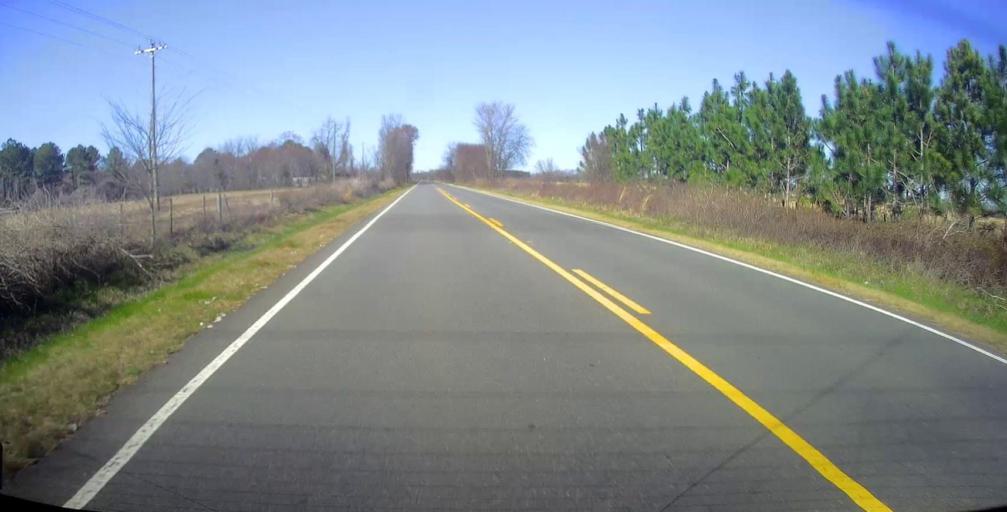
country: US
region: Georgia
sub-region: Macon County
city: Montezuma
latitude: 32.3786
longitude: -84.0148
